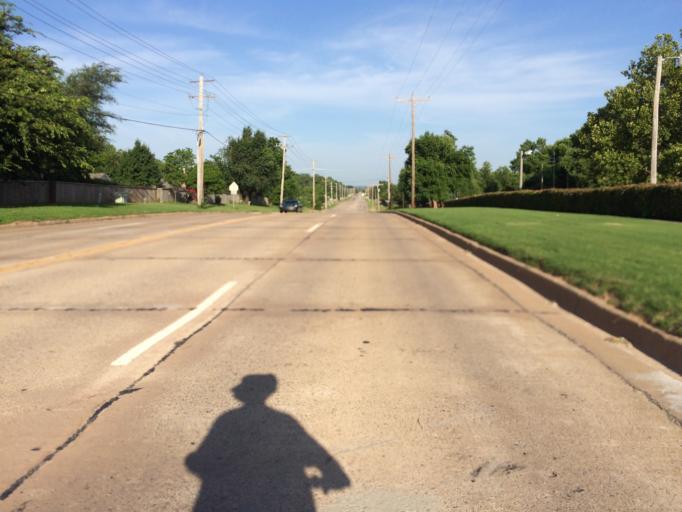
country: US
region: Oklahoma
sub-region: Cleveland County
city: Norman
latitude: 35.2184
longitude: -97.5013
